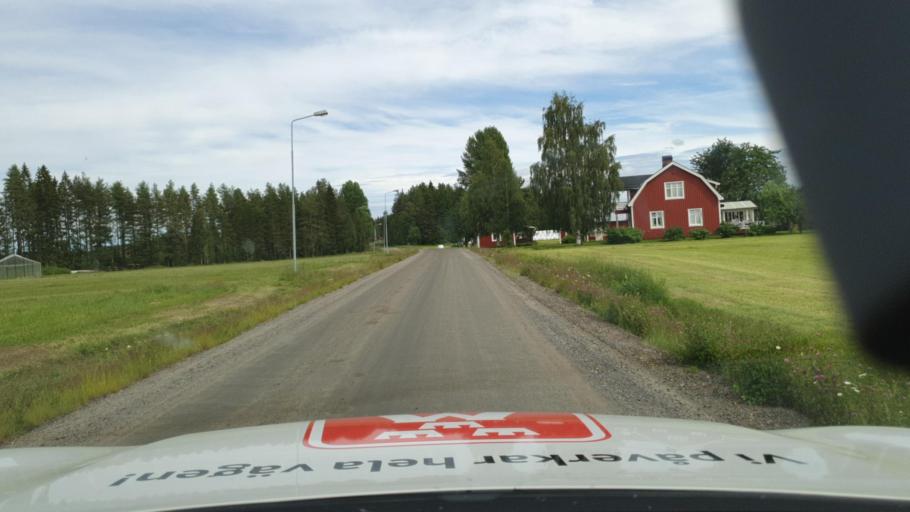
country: SE
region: Vaesterbotten
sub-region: Skelleftea Kommun
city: Viken
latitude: 64.5000
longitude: 20.9129
